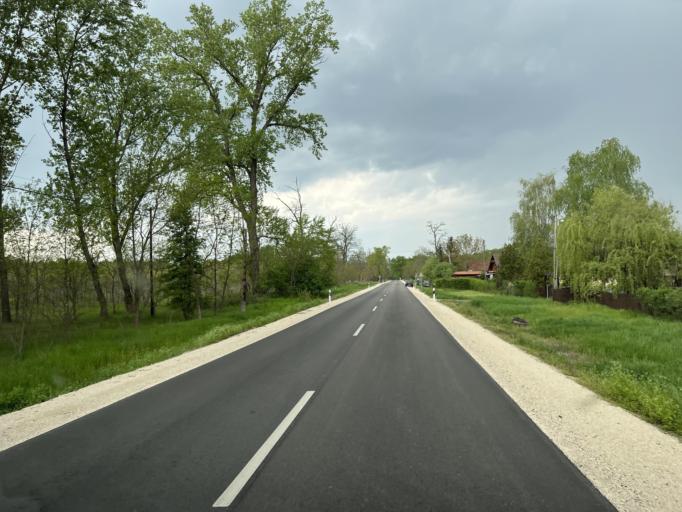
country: HU
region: Pest
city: Nagykoros
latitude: 47.0542
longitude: 19.7216
